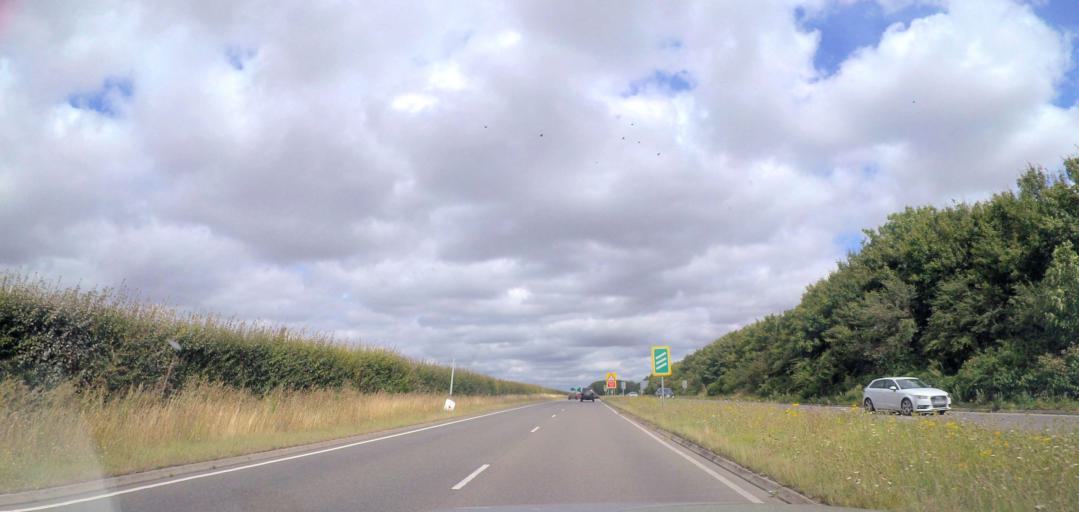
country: GB
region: England
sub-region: Hertfordshire
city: Royston
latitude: 52.0594
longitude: -0.0344
